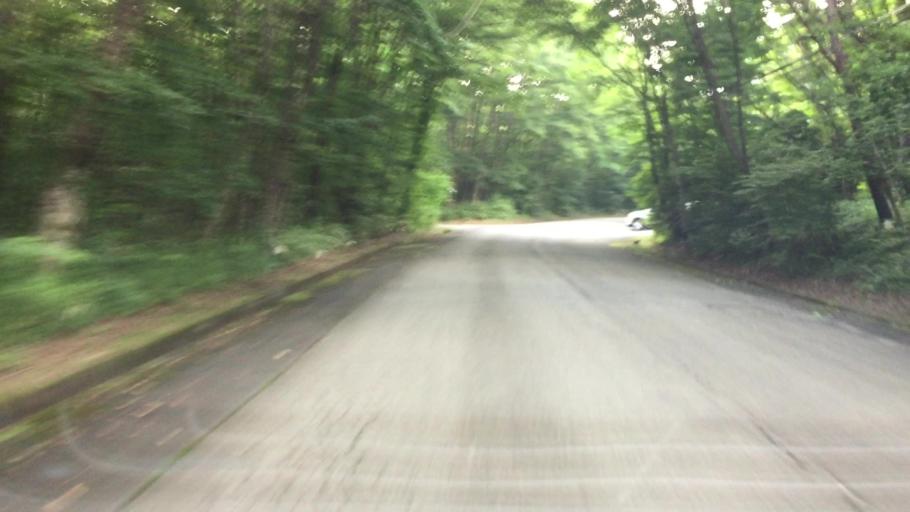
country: JP
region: Tochigi
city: Kuroiso
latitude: 37.1090
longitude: 140.0374
